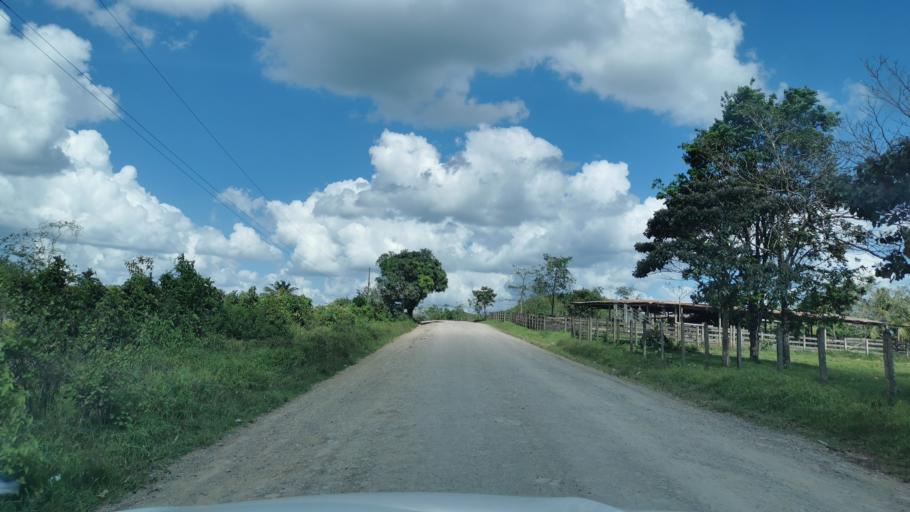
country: NI
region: Atlantico Sur
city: Rama
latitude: 12.1711
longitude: -84.2049
